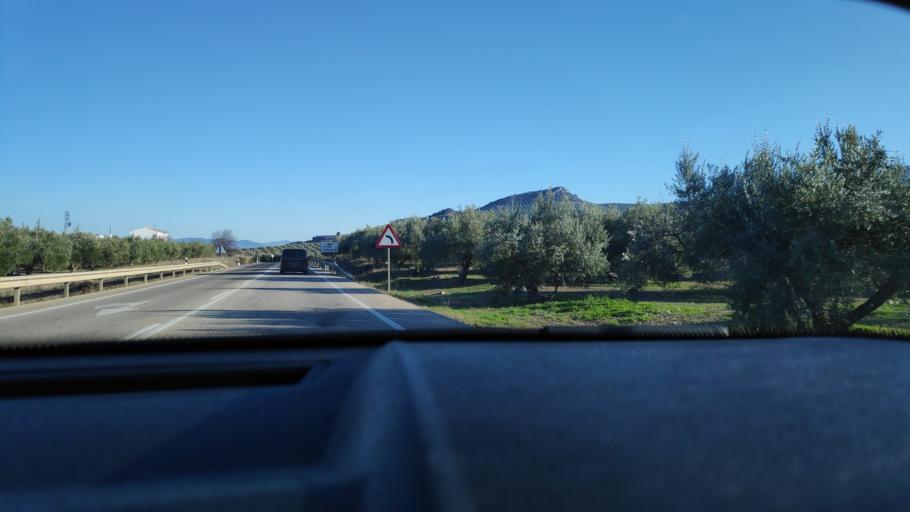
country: ES
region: Andalusia
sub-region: Province of Cordoba
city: Luque
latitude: 37.5655
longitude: -4.2269
